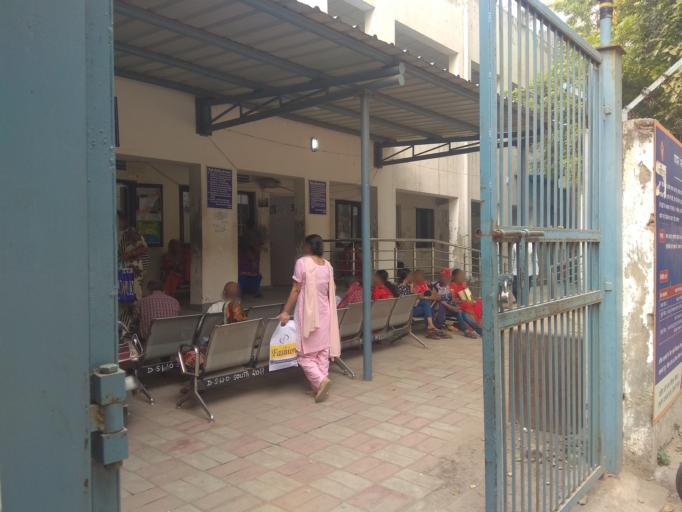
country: IN
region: NCT
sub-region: New Delhi
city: New Delhi
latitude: 28.5724
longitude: 77.2448
